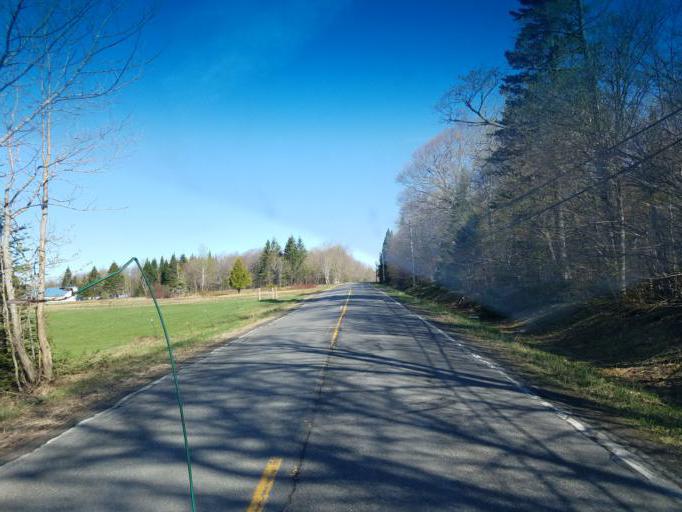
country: US
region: Maine
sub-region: Aroostook County
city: Caribou
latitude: 46.8722
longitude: -68.2141
